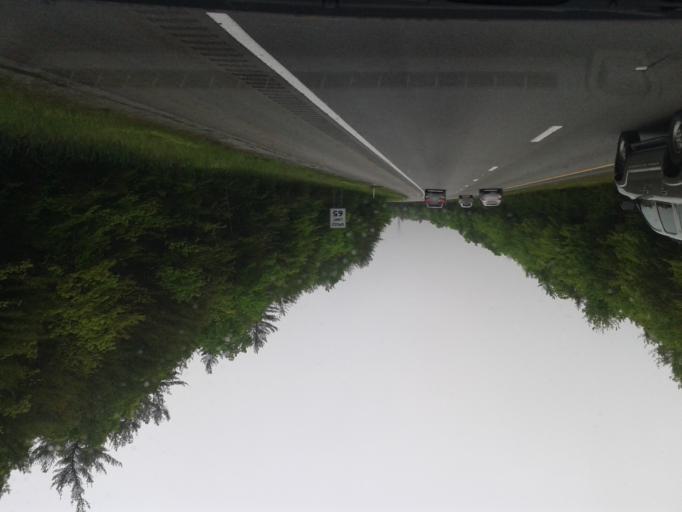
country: US
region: Massachusetts
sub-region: Plymouth County
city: Mattapoisett Center
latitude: 41.6963
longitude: -70.8023
